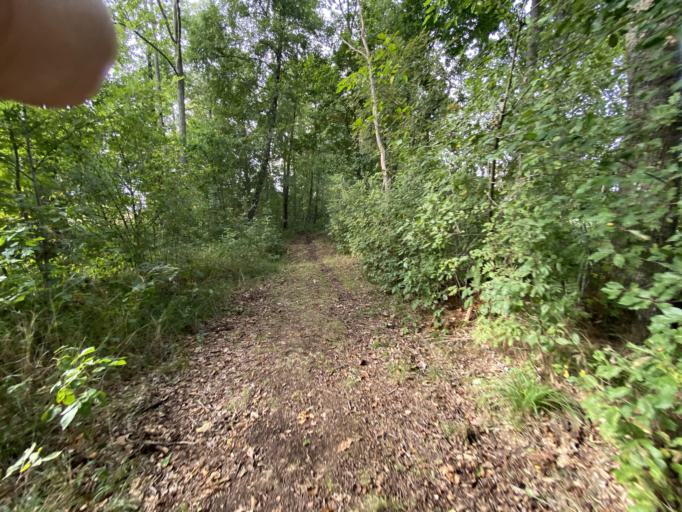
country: SE
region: Skane
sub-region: Hassleholms Kommun
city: Hastveda
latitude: 56.3629
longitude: 13.8834
